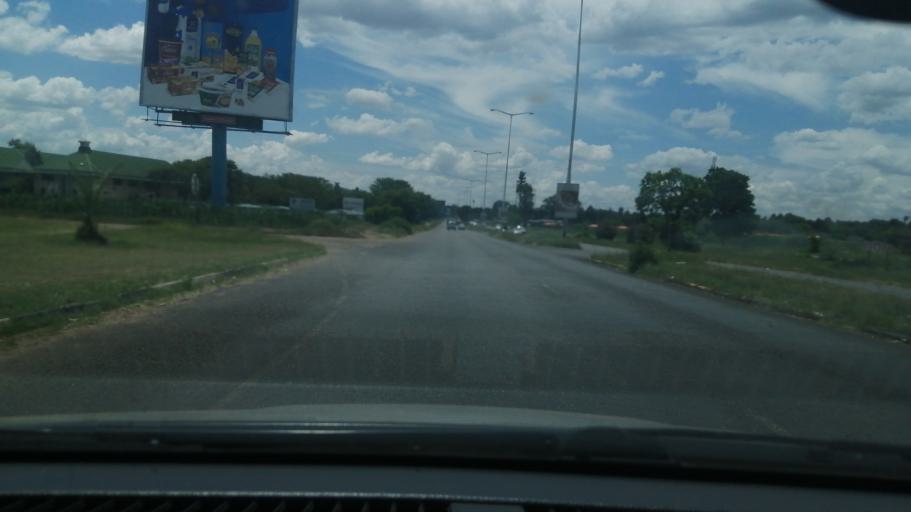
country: ZW
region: Harare
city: Harare
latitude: -17.8225
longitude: 31.0836
